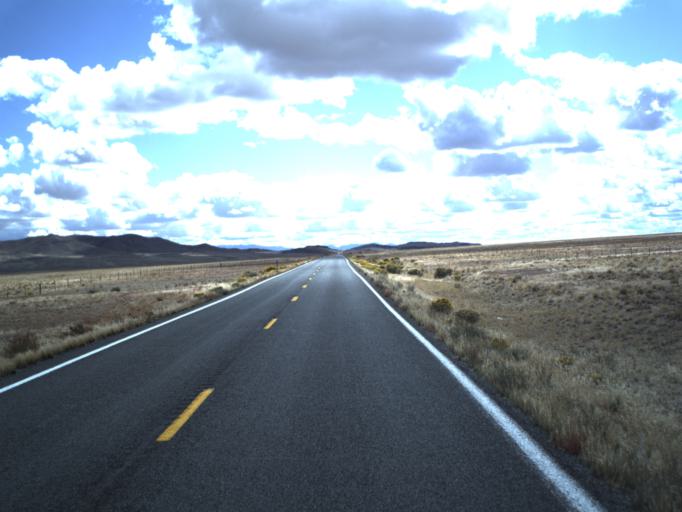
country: US
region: Utah
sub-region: Beaver County
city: Milford
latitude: 38.6772
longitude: -113.8897
